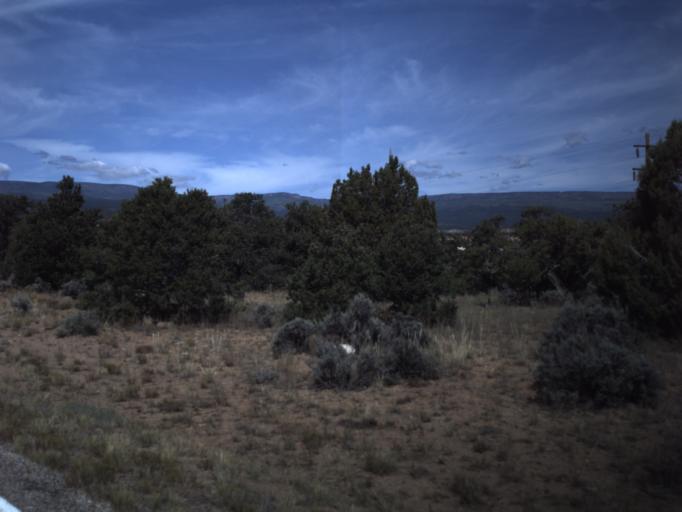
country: US
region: Utah
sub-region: Wayne County
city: Loa
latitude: 37.8711
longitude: -111.4435
